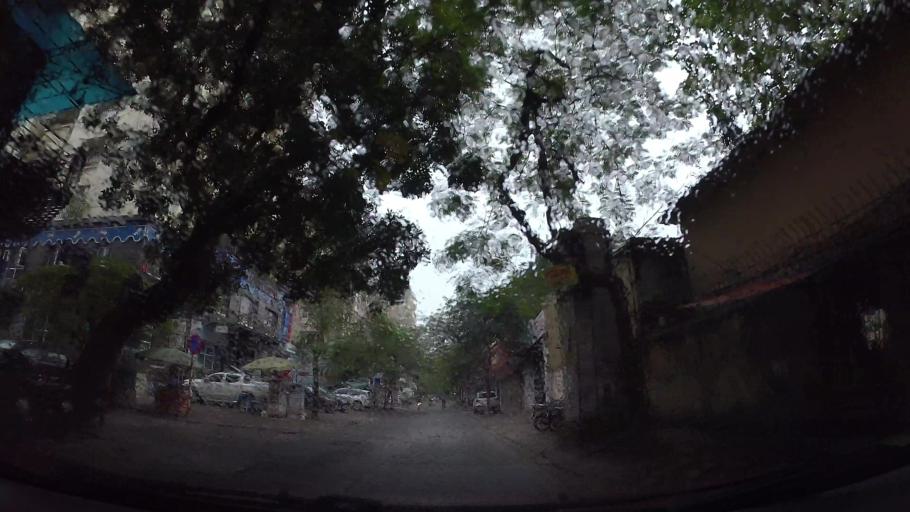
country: VN
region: Ha Noi
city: Dong Da
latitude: 21.0140
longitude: 105.8148
